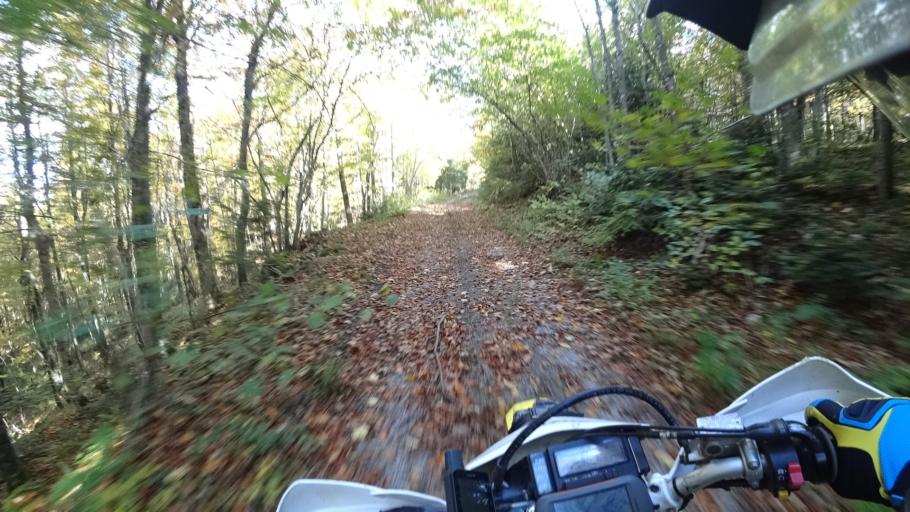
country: HR
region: Karlovacka
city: Plaski
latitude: 45.0719
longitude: 15.3224
